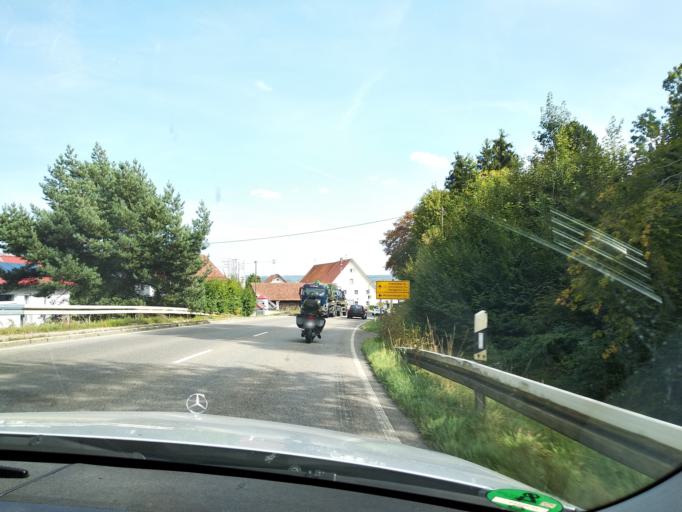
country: DE
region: Baden-Wuerttemberg
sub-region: Tuebingen Region
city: Berg
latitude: 47.8526
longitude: 9.6010
